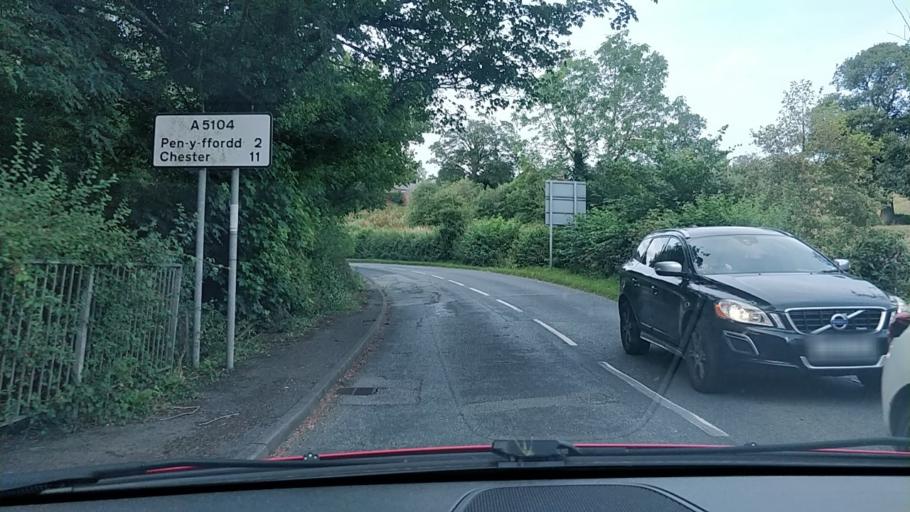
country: GB
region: Wales
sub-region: County of Flintshire
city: Leeswood
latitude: 53.1376
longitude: -3.0826
